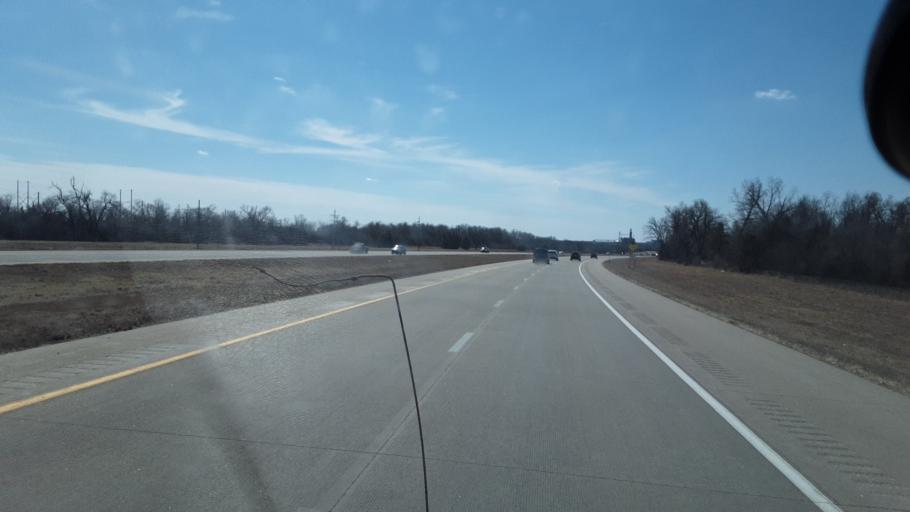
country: US
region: Kansas
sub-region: Reno County
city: Hutchinson
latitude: 38.0959
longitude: -97.8764
